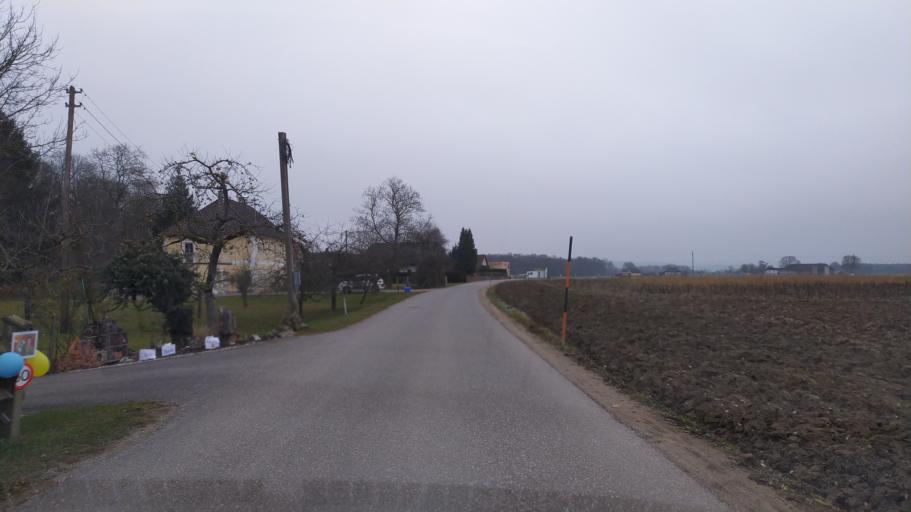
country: AT
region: Upper Austria
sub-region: Politischer Bezirk Perg
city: Perg
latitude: 48.2055
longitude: 14.7139
